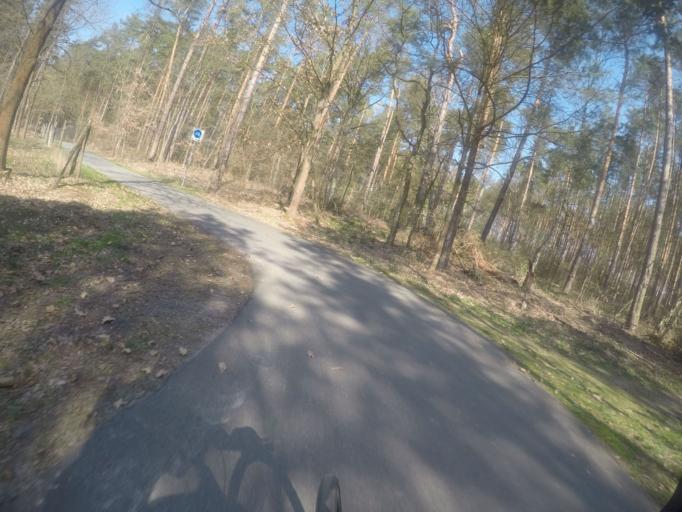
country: DE
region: Brandenburg
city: Brieselang
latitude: 52.6469
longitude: 13.0218
